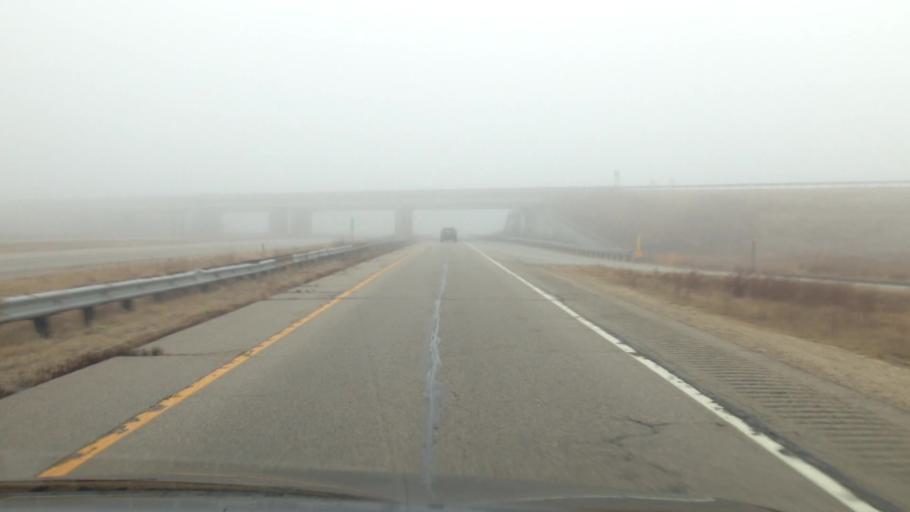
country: US
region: Wisconsin
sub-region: Walworth County
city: Elkhorn
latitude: 42.6685
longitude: -88.5171
